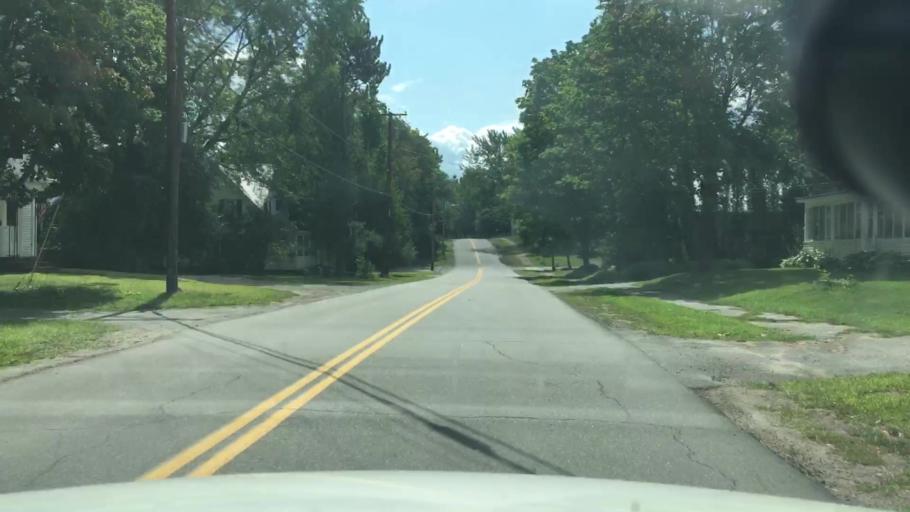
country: US
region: Maine
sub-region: Somerset County
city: Skowhegan
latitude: 44.7578
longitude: -69.7170
